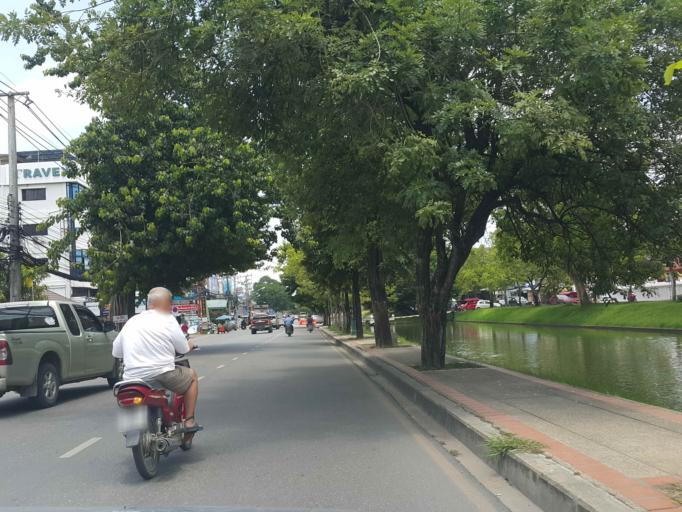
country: TH
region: Chiang Mai
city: Chiang Mai
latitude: 18.7958
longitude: 98.9830
